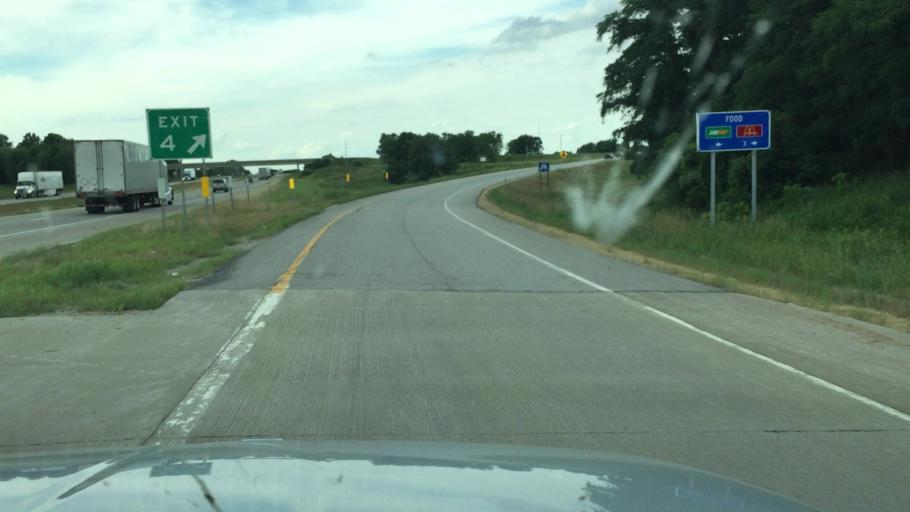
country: US
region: Iowa
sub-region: Scott County
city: Buffalo
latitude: 41.5343
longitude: -90.6755
